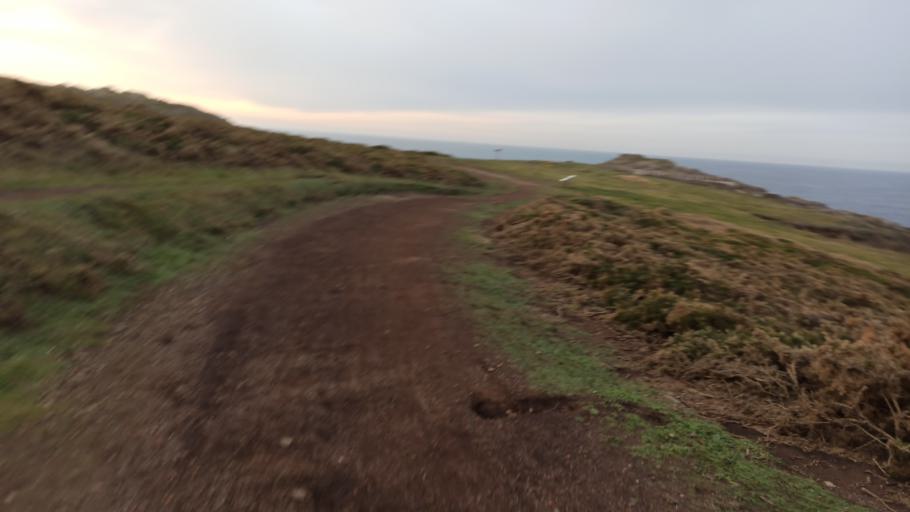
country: ES
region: Galicia
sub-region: Provincia da Coruna
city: A Coruna
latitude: 43.3961
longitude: -8.3451
